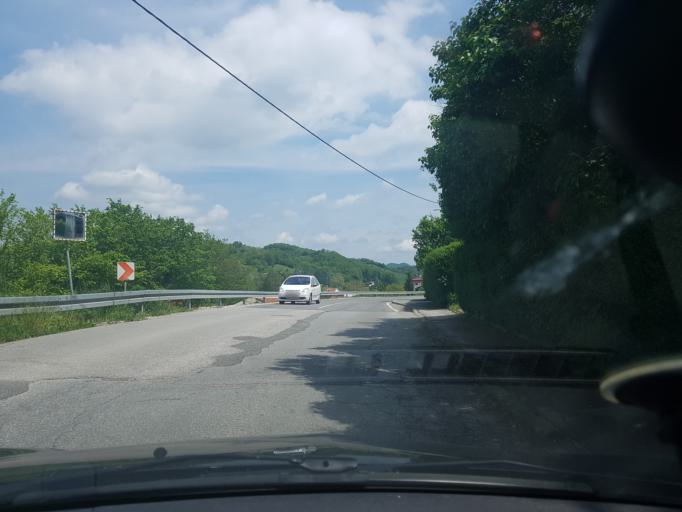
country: SI
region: Rogatec
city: Rogatec
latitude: 46.2220
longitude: 15.6952
